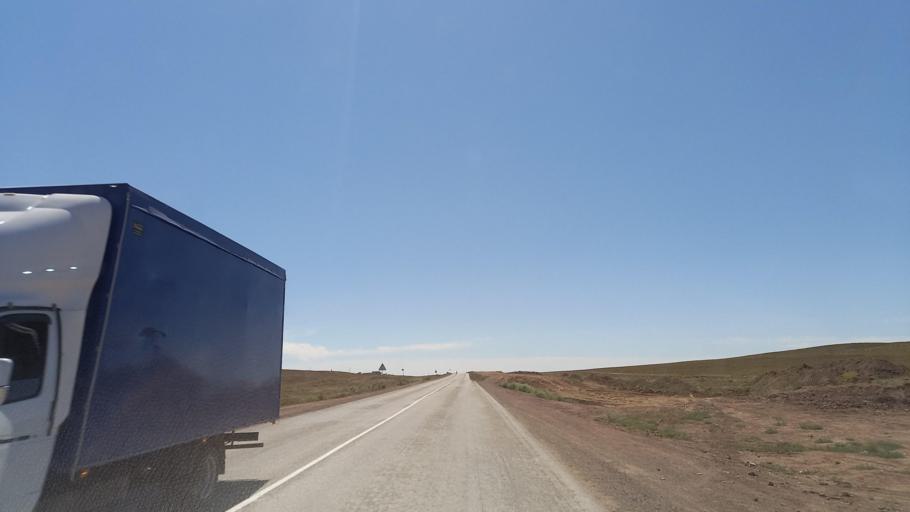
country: KZ
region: Zhambyl
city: Mynaral
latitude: 45.3321
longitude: 73.7248
